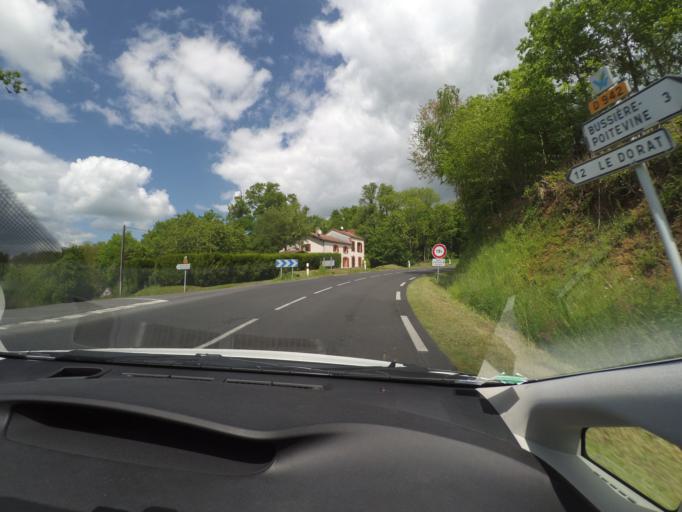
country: FR
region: Limousin
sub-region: Departement de la Haute-Vienne
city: Bussiere-Poitevine
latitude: 46.2338
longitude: 0.9345
